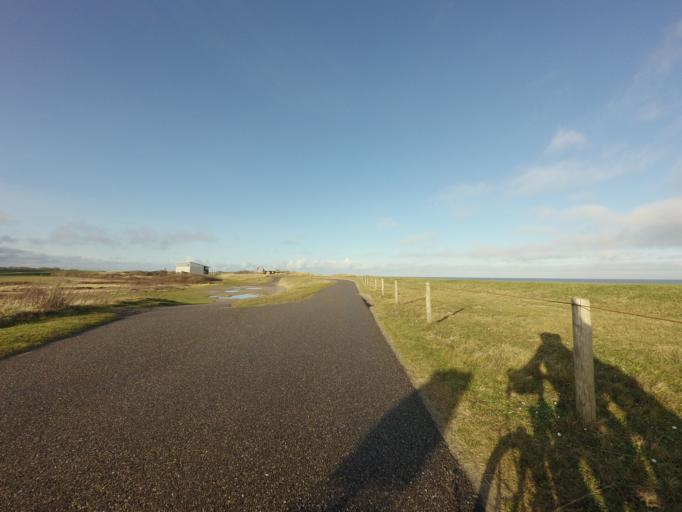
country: NL
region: North Holland
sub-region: Gemeente Texel
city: Den Burg
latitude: 53.1730
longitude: 4.8720
